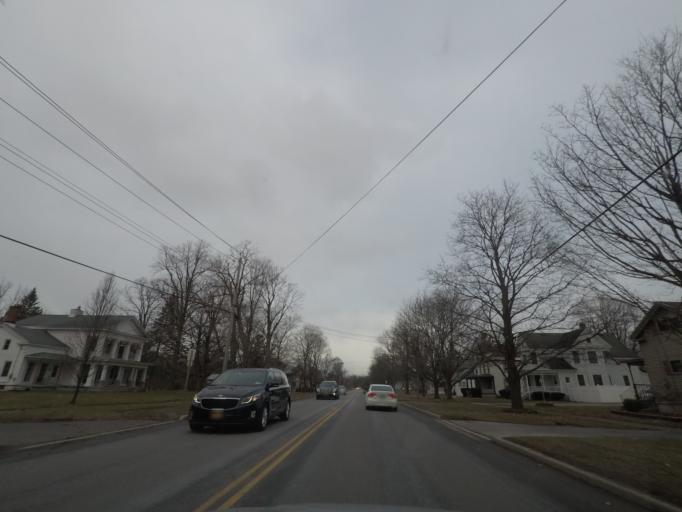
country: US
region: New York
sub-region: Madison County
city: Oneida
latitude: 43.0775
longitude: -75.6309
